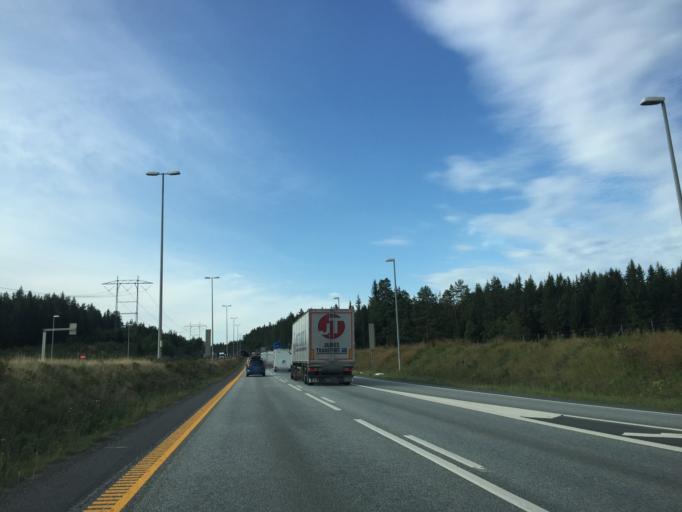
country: NO
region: Akershus
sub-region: Oppegard
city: Kolbotn
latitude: 59.7947
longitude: 10.8419
